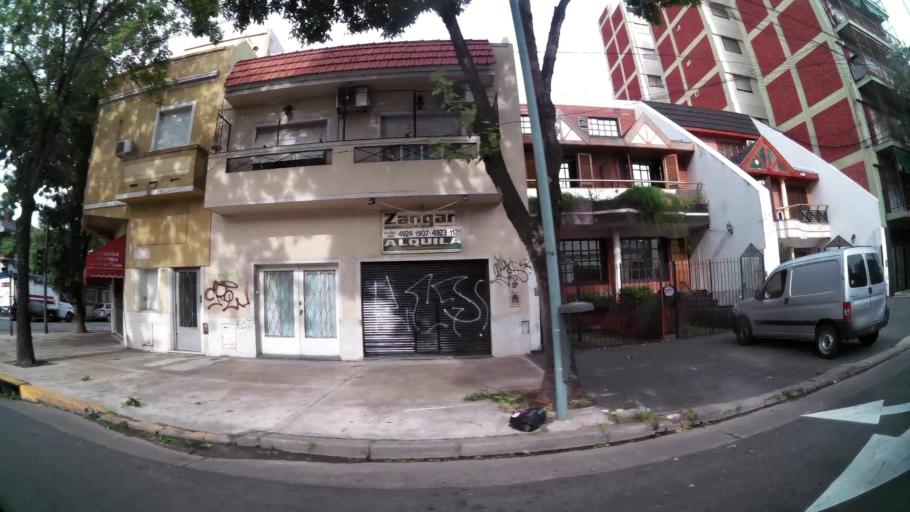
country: AR
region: Buenos Aires F.D.
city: Villa Santa Rita
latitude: -34.6371
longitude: -58.4319
